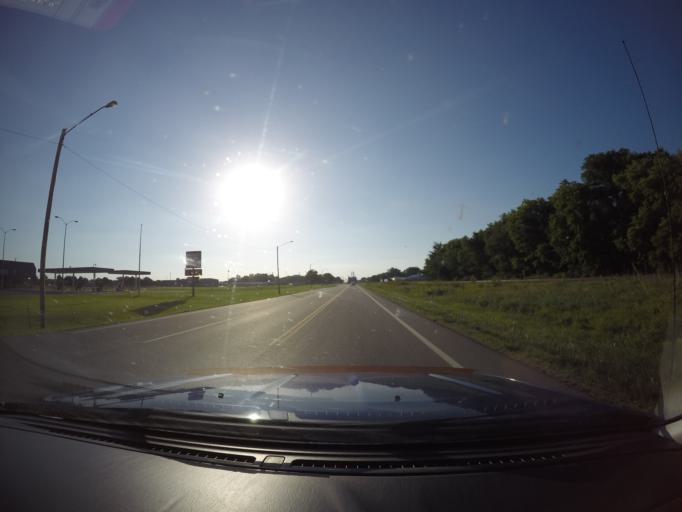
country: US
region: Kansas
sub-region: Shawnee County
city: Rossville
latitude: 39.1320
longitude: -95.9441
